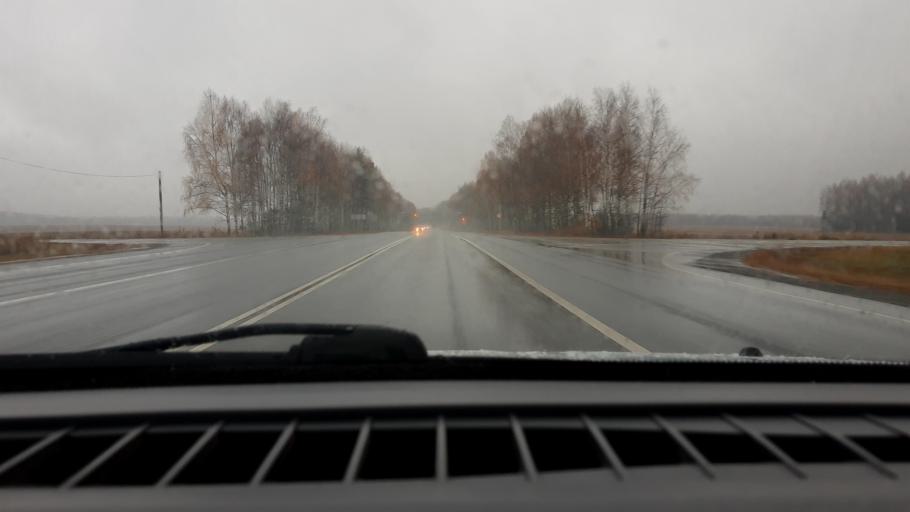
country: RU
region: Nizjnij Novgorod
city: Linda
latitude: 56.6560
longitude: 44.1217
